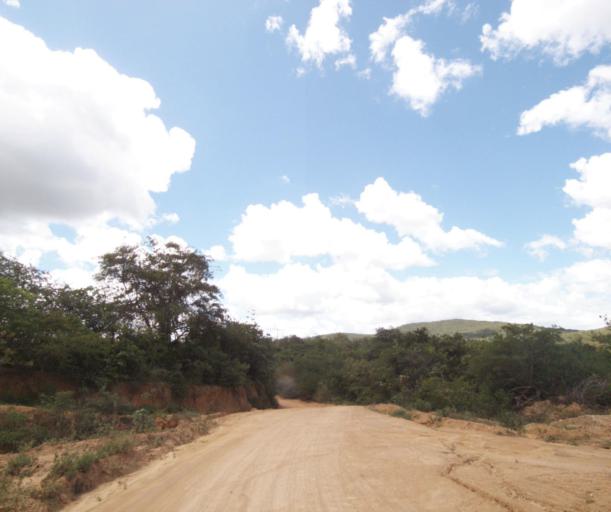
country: BR
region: Bahia
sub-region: Pocoes
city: Pocoes
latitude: -14.3893
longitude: -40.5489
